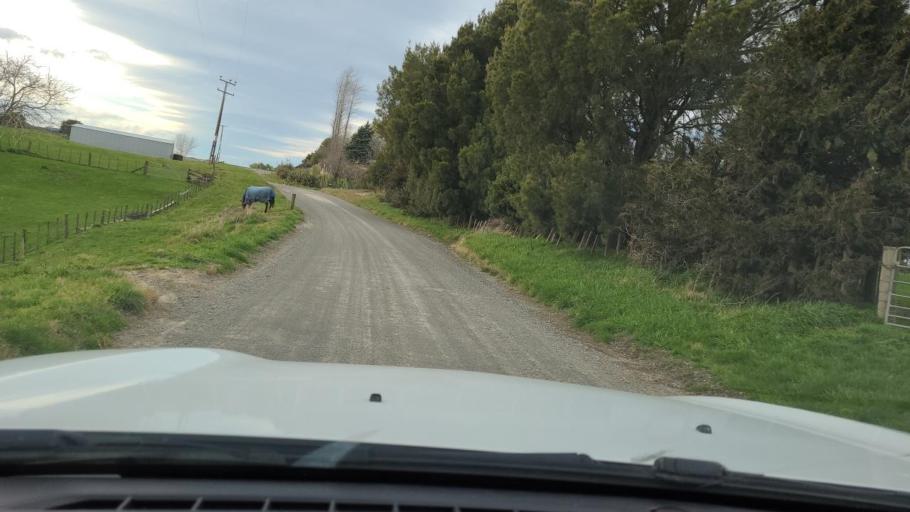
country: NZ
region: Hawke's Bay
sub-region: Napier City
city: Napier
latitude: -39.3212
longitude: 176.8378
